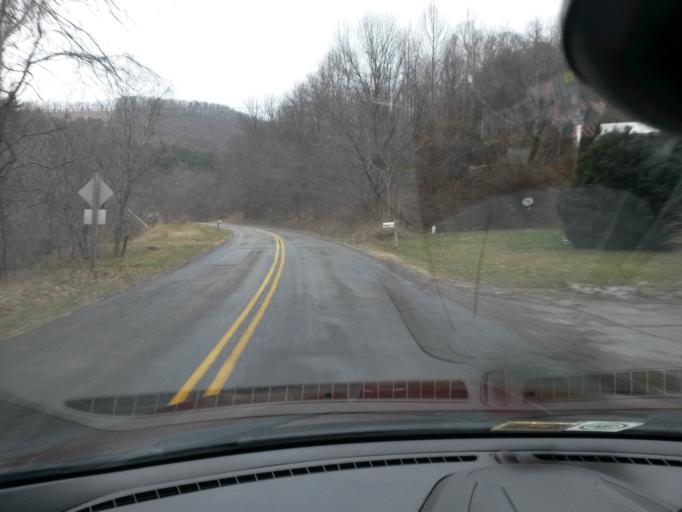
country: US
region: Virginia
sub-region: City of Lexington
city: Lexington
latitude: 37.8929
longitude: -79.5723
